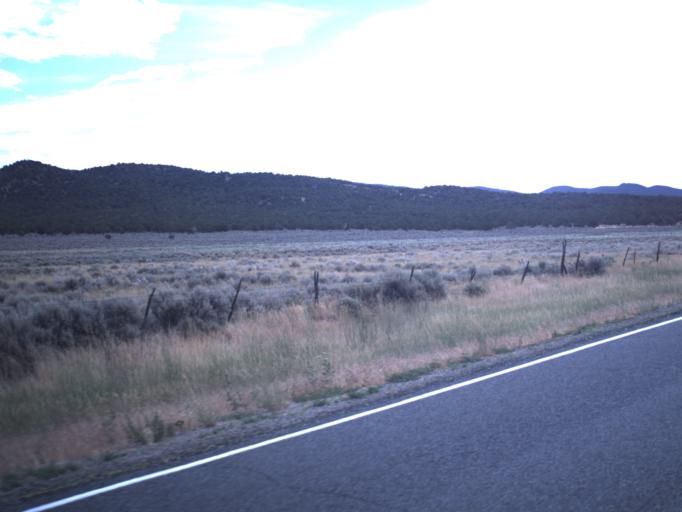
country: US
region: Utah
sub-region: Beaver County
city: Beaver
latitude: 38.6057
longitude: -112.5868
